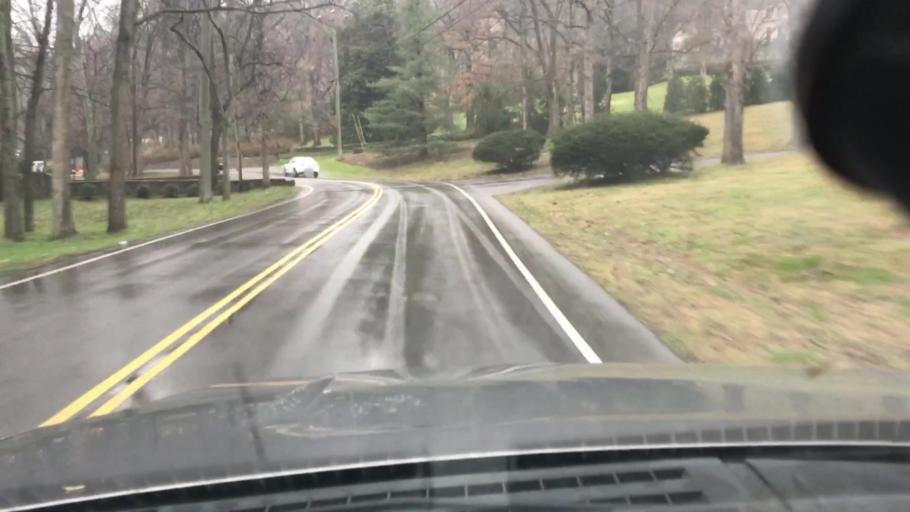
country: US
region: Tennessee
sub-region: Davidson County
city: Forest Hills
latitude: 36.0703
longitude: -86.8606
